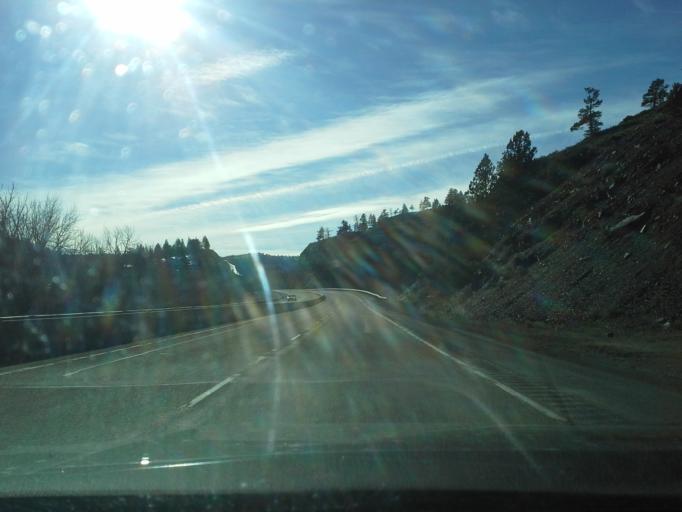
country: US
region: Montana
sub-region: Lewis and Clark County
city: Helena Valley Northwest
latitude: 46.9444
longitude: -112.1216
